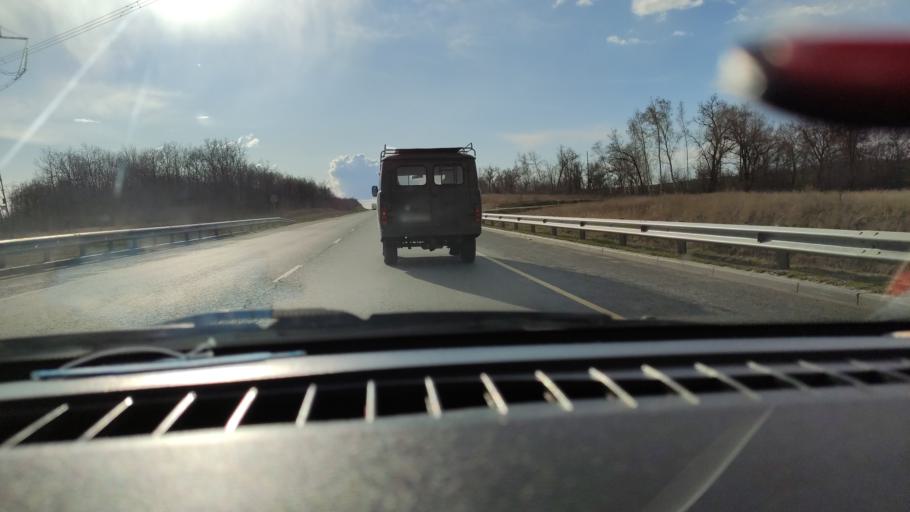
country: RU
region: Saratov
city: Yelshanka
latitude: 51.8238
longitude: 46.3126
